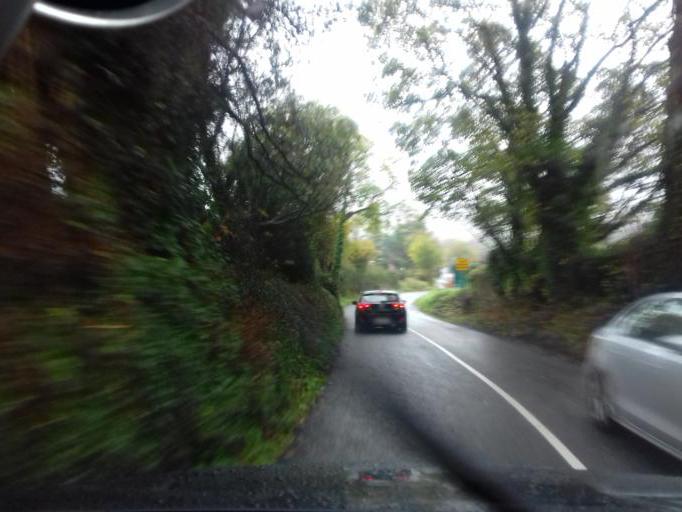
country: IE
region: Leinster
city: Ballyboden
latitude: 53.2627
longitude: -6.3104
